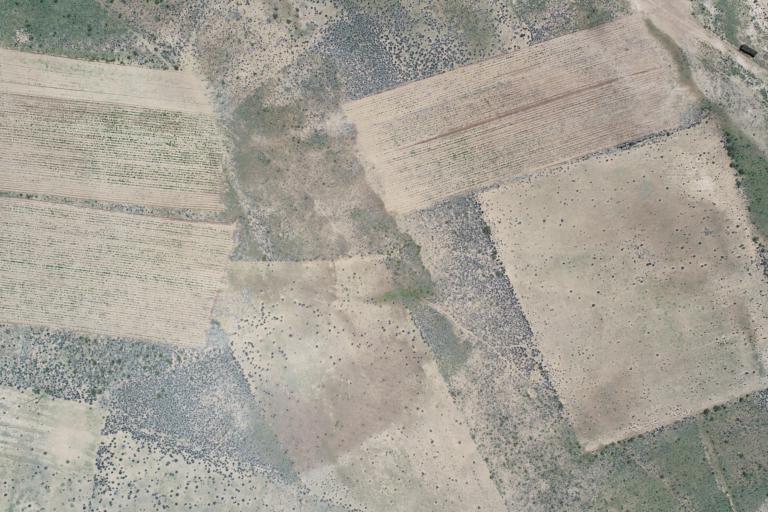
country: BO
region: La Paz
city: Curahuara de Carangas
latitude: -17.3110
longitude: -68.5086
